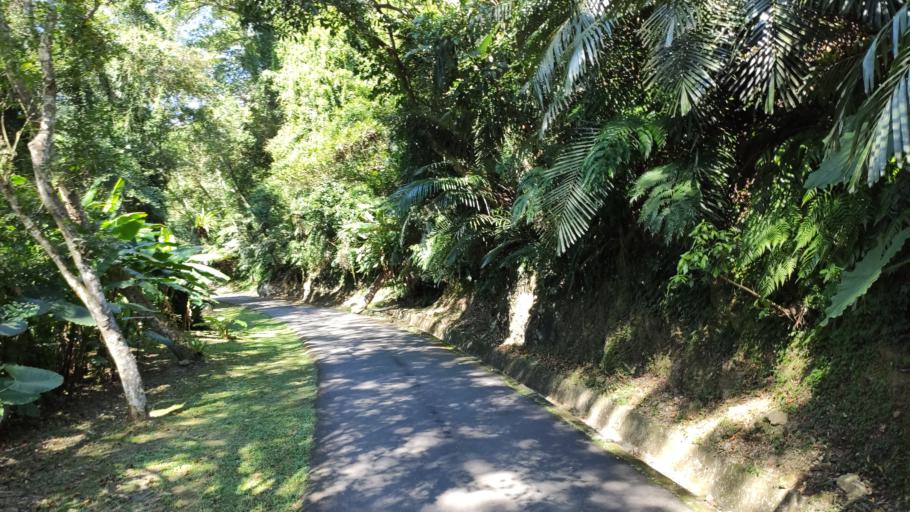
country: TW
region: Taiwan
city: Daxi
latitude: 24.8417
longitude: 121.3053
